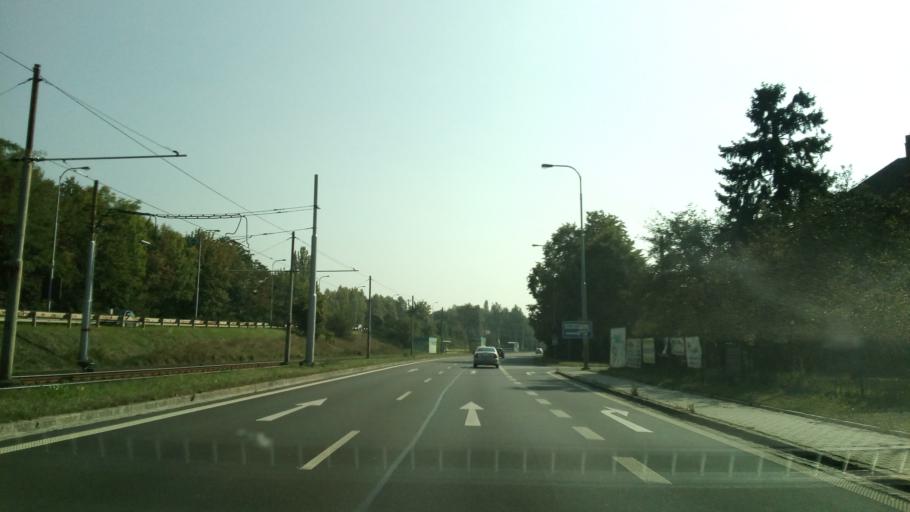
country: CZ
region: Moravskoslezsky
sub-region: Okres Ostrava-Mesto
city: Ostrava
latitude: 49.8121
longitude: 18.2417
